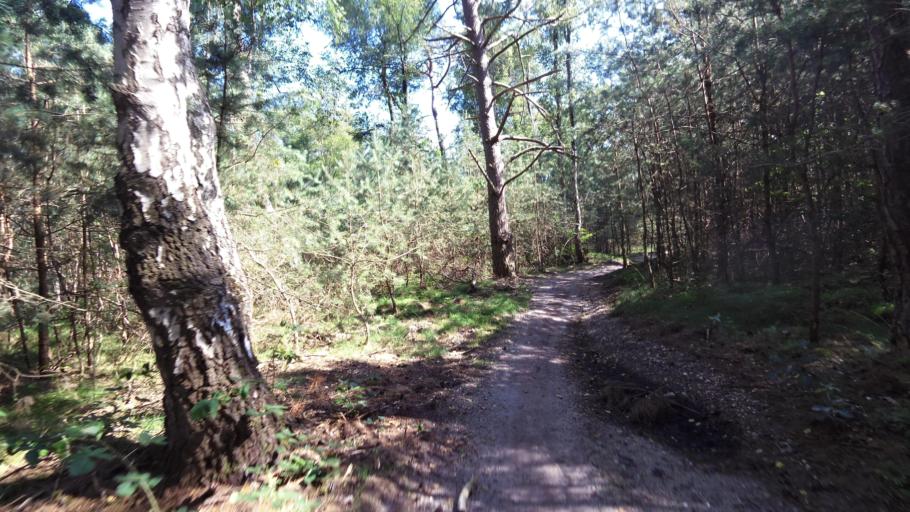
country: NL
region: Gelderland
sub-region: Gemeente Arnhem
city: Gulden Bodem
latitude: 52.0218
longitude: 5.9166
